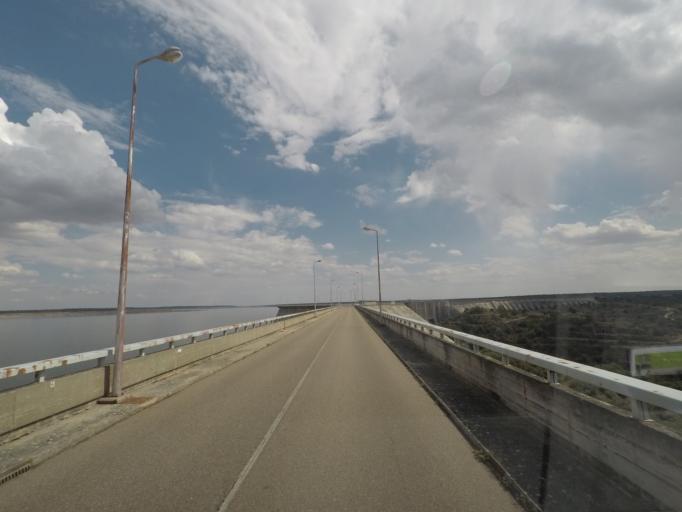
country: ES
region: Castille and Leon
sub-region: Provincia de Salamanca
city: Almendra
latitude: 41.2746
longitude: -6.3251
